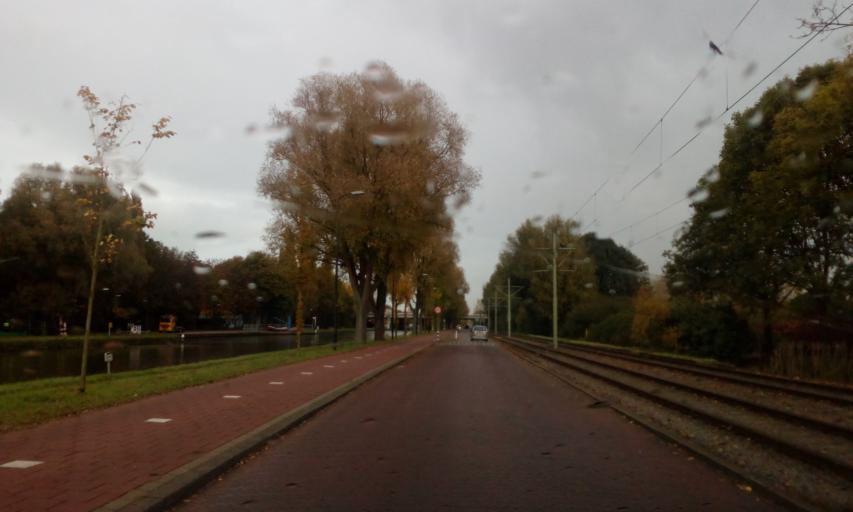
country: NL
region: South Holland
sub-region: Gemeente Rijswijk
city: Rijswijk
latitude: 52.0372
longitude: 4.3454
